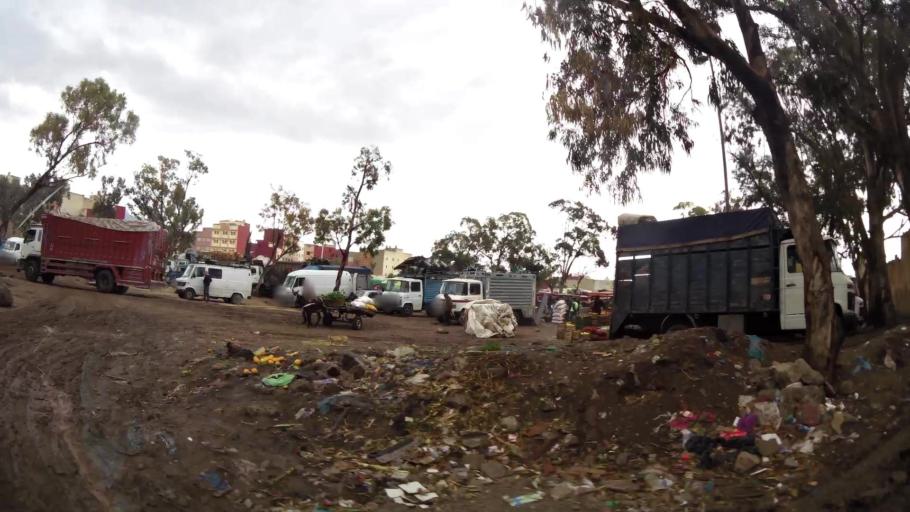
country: MA
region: Oriental
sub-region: Nador
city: Nador
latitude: 35.1514
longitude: -3.0054
